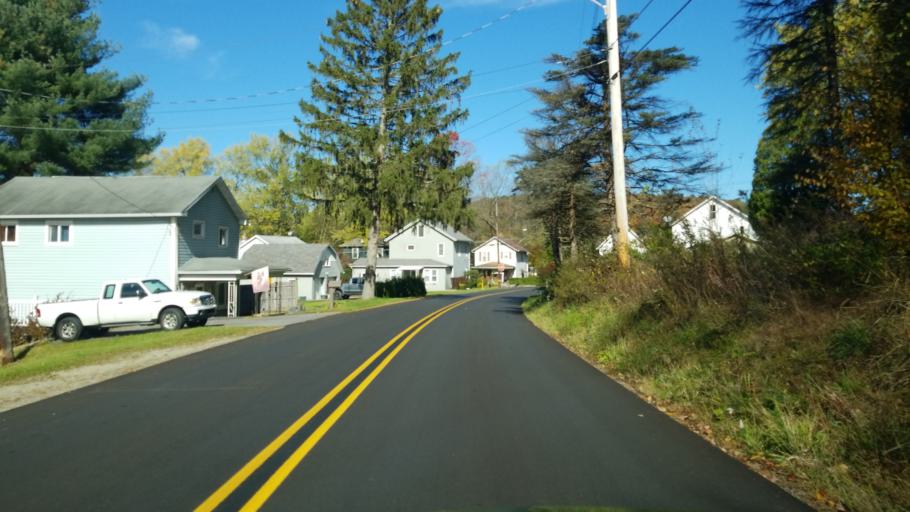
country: US
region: Pennsylvania
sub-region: Jefferson County
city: Brockway
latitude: 41.2458
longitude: -78.7960
